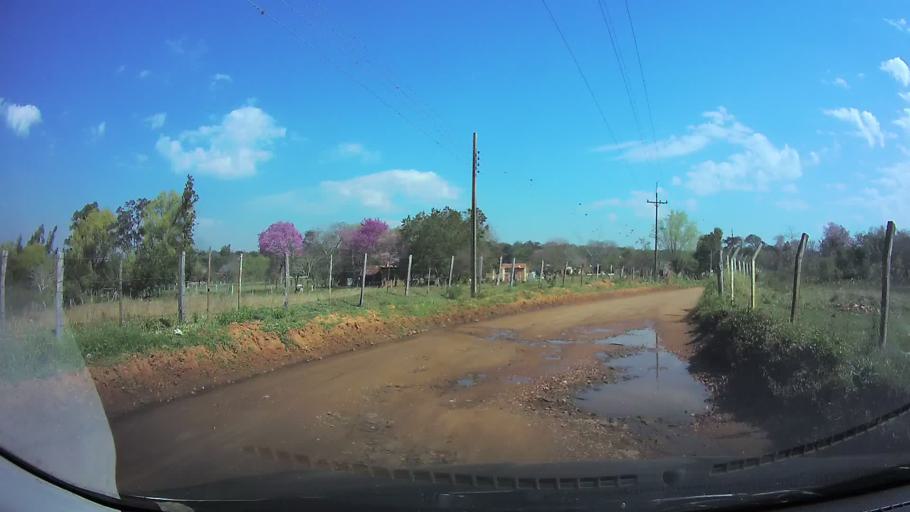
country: PY
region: Central
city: Limpio
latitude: -25.2322
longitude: -57.4441
